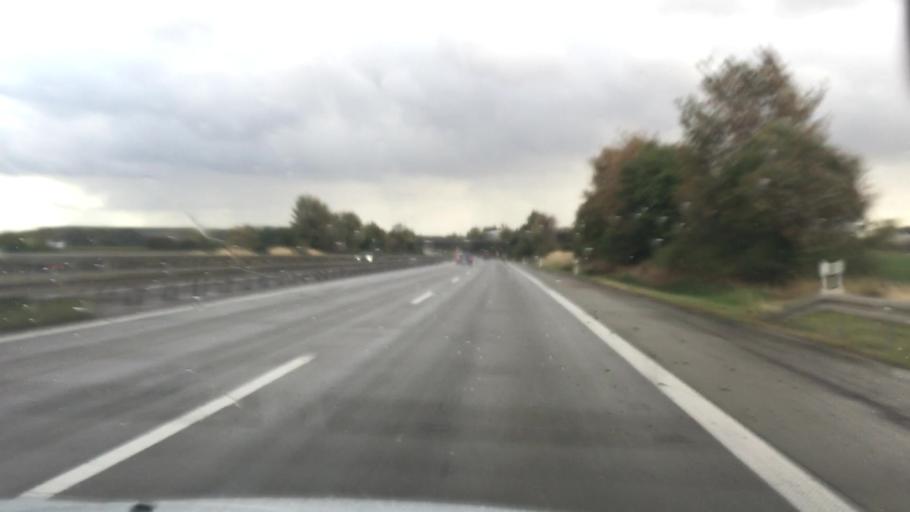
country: DE
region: Saxony-Anhalt
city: Hohendodeleben
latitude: 52.1217
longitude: 11.5296
